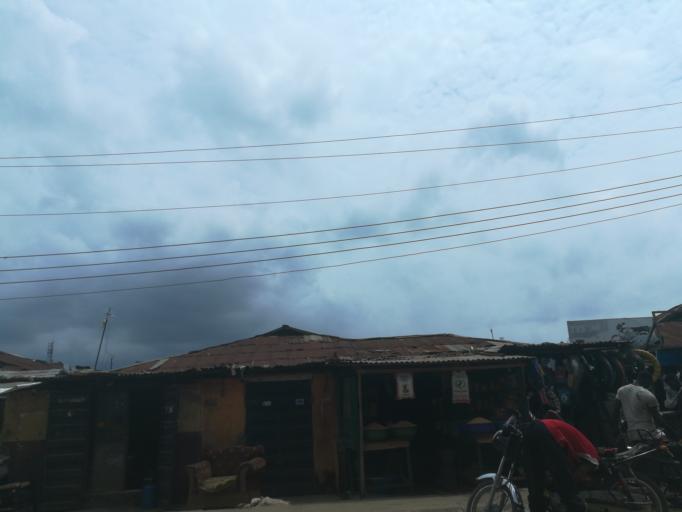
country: NG
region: Lagos
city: Somolu
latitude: 6.5327
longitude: 3.3930
